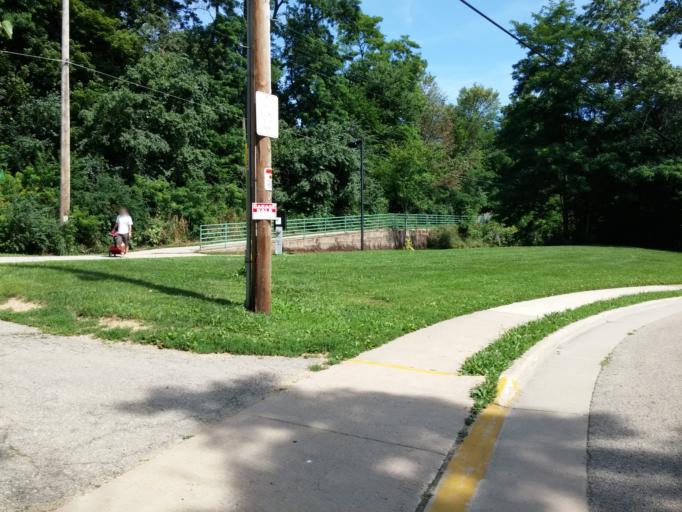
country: US
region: Wisconsin
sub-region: Dane County
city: Shorewood Hills
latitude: 43.0607
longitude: -89.4285
